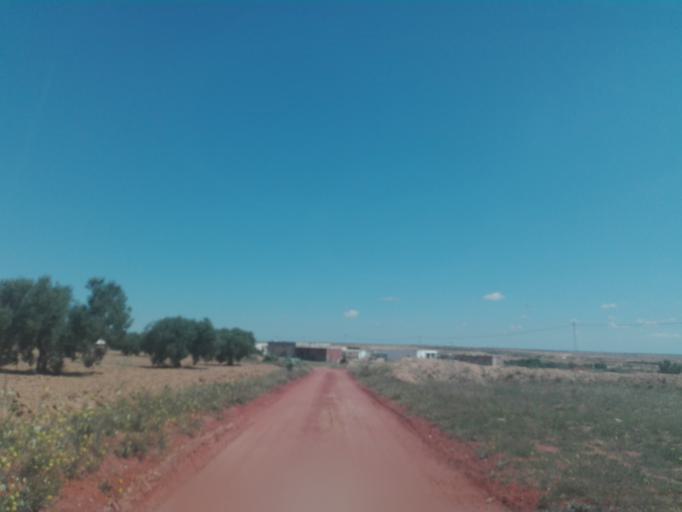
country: TN
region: Safaqis
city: Sfax
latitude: 34.7325
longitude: 10.4331
